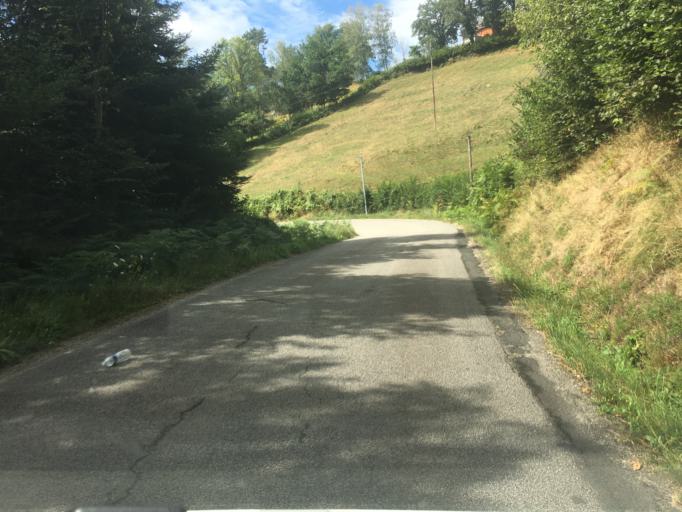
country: FR
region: Auvergne
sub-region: Departement du Cantal
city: Champagnac
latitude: 45.4389
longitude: 2.3985
